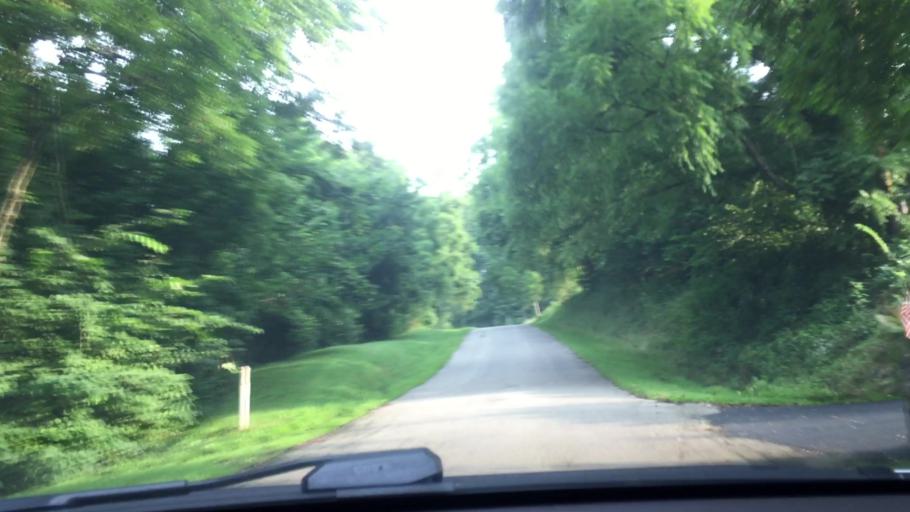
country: US
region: Pennsylvania
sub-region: Washington County
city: McMurray
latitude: 40.1769
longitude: -80.1036
